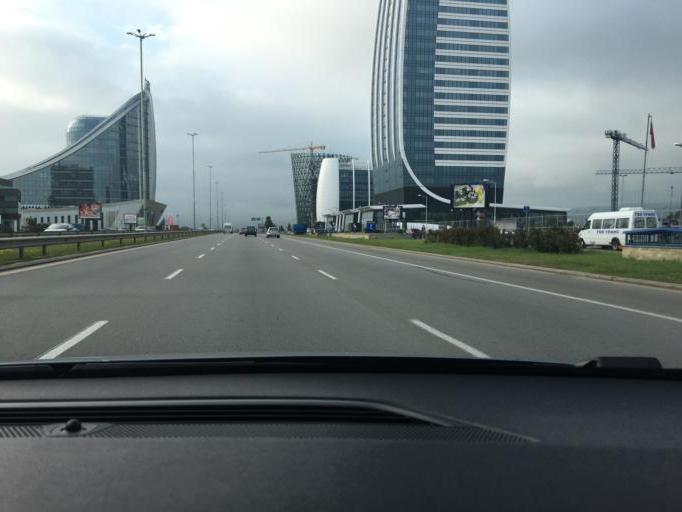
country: BG
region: Sofia-Capital
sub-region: Stolichna Obshtina
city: Sofia
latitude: 42.6486
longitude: 23.3947
